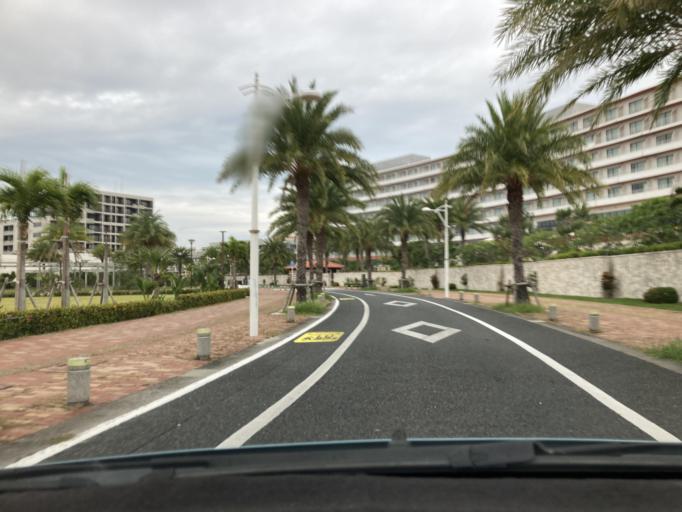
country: JP
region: Okinawa
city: Chatan
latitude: 26.3183
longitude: 127.7538
